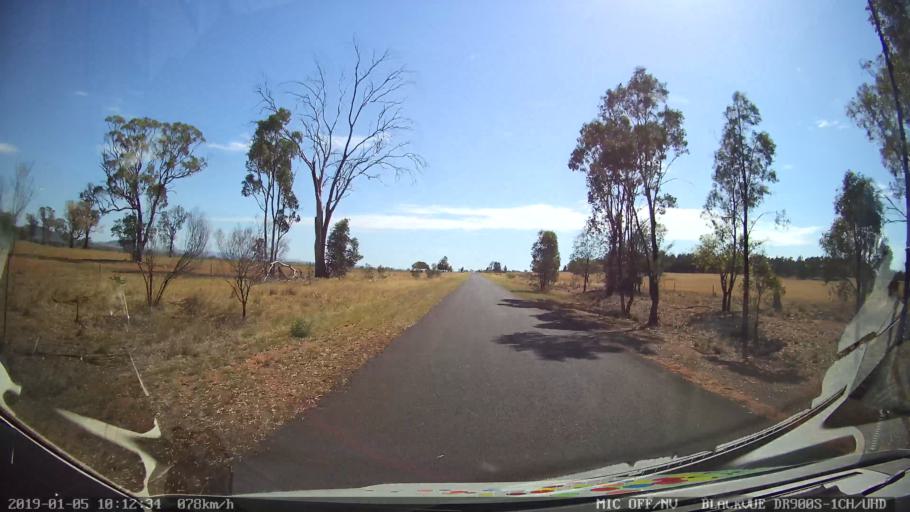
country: AU
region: New South Wales
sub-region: Gilgandra
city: Gilgandra
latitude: -31.6070
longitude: 148.9144
